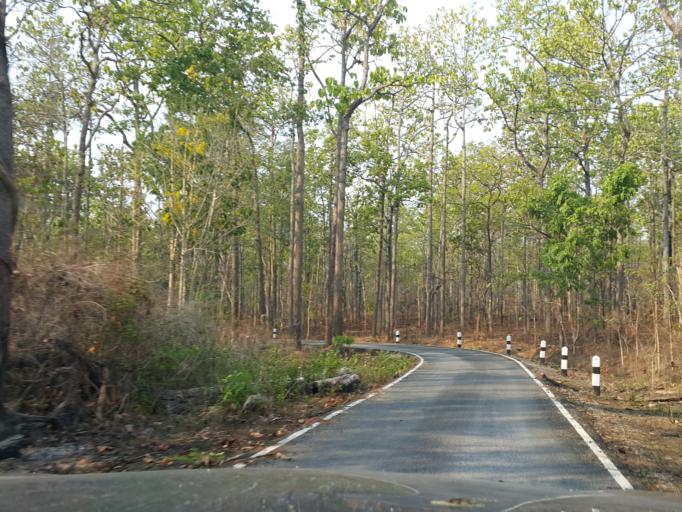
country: TH
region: Lamphun
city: Li
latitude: 17.6225
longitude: 98.8707
